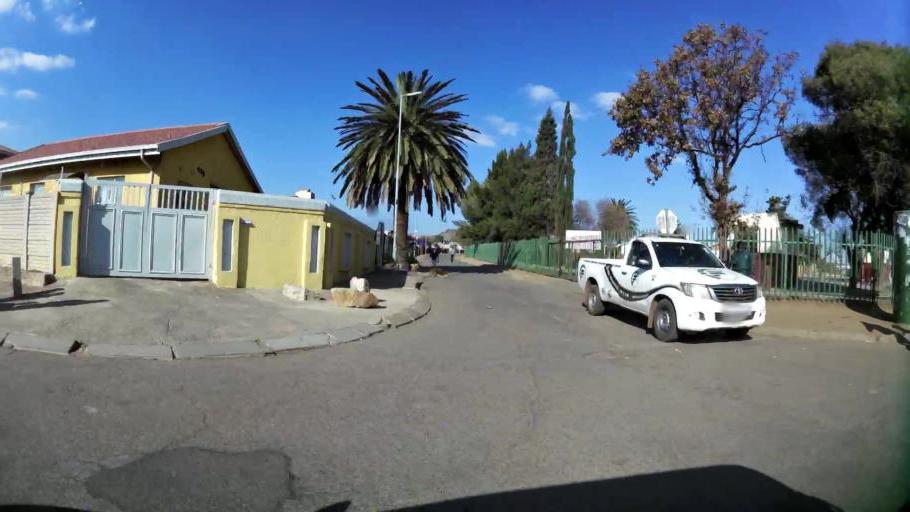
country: ZA
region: Gauteng
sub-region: City of Johannesburg Metropolitan Municipality
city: Soweto
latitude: -26.2583
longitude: 27.9089
